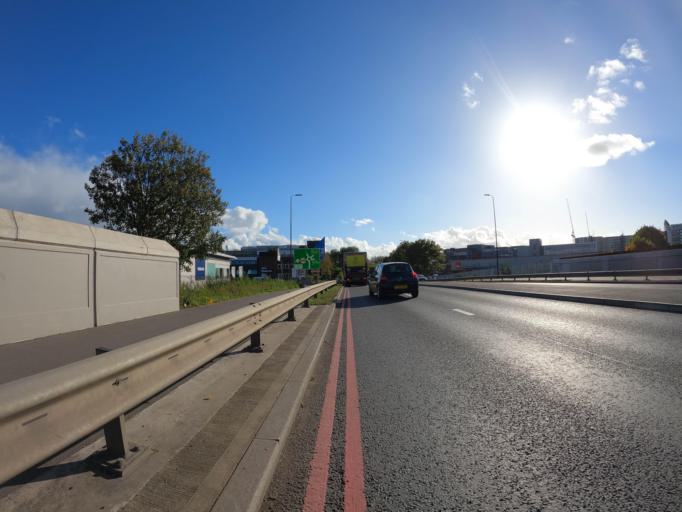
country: GB
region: England
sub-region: Greater London
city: Acton
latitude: 51.4940
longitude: -0.2823
